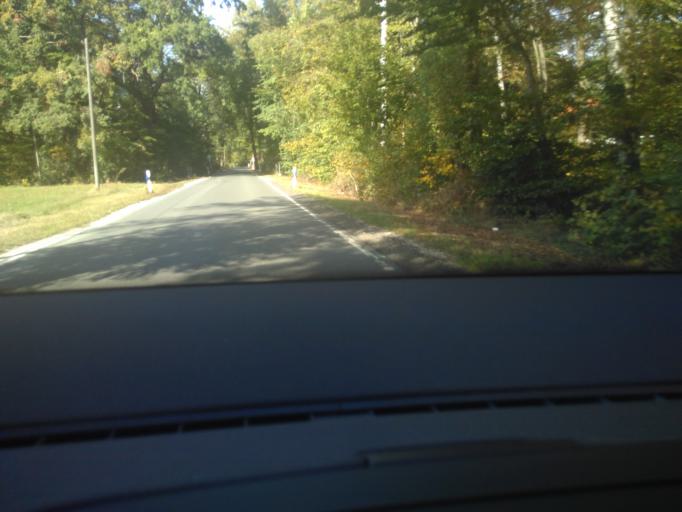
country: DE
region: North Rhine-Westphalia
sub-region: Regierungsbezirk Detmold
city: Verl
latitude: 51.9255
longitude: 8.5118
